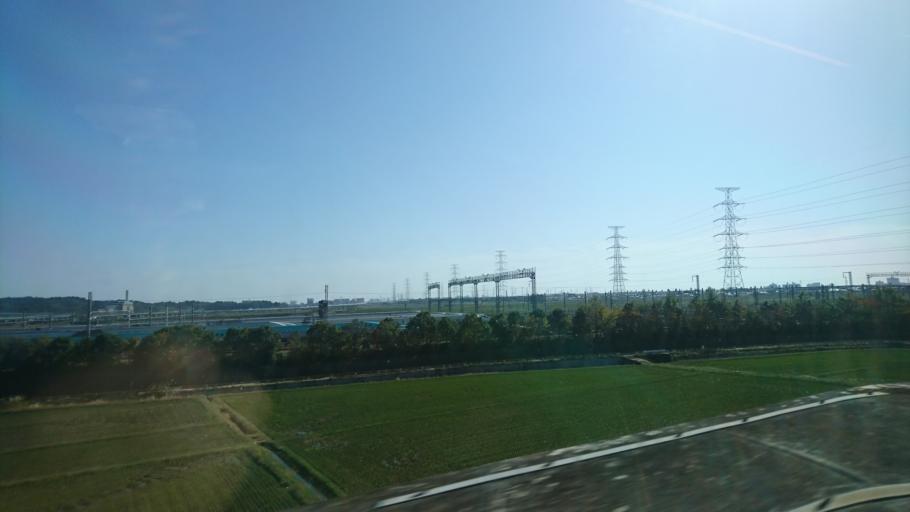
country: JP
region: Miyagi
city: Rifu
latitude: 38.3133
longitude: 140.9655
